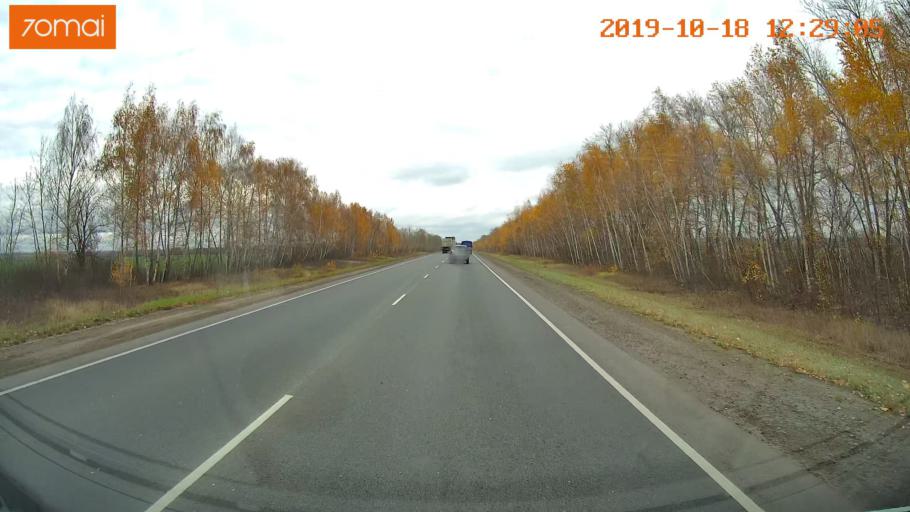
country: RU
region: Rjazan
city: Ryazan'
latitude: 54.5763
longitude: 39.5790
